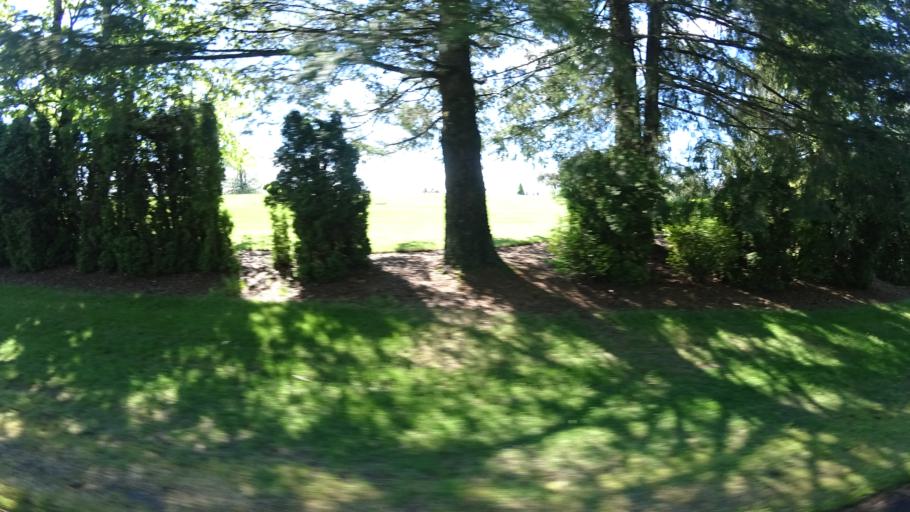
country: US
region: Oregon
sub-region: Washington County
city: West Haven
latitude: 45.5555
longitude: -122.7788
